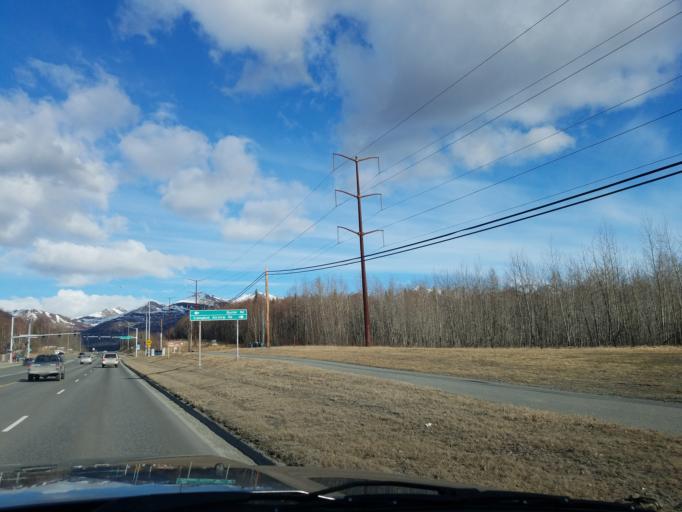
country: US
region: Alaska
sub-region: Anchorage Municipality
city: Anchorage
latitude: 61.1807
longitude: -149.7666
